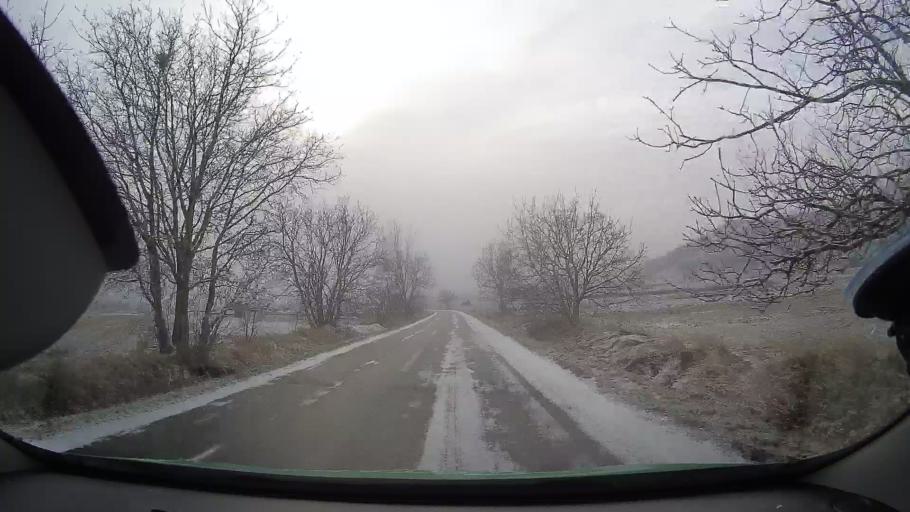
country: RO
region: Alba
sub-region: Comuna Rimetea
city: Rimetea
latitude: 46.4155
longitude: 23.5580
